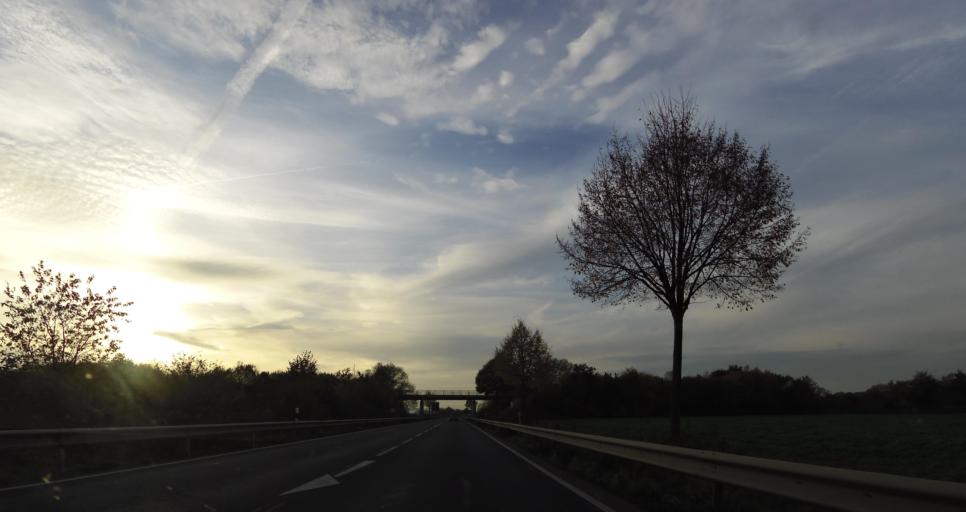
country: DE
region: Lower Saxony
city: Einbeck
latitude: 51.8044
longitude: 9.8689
